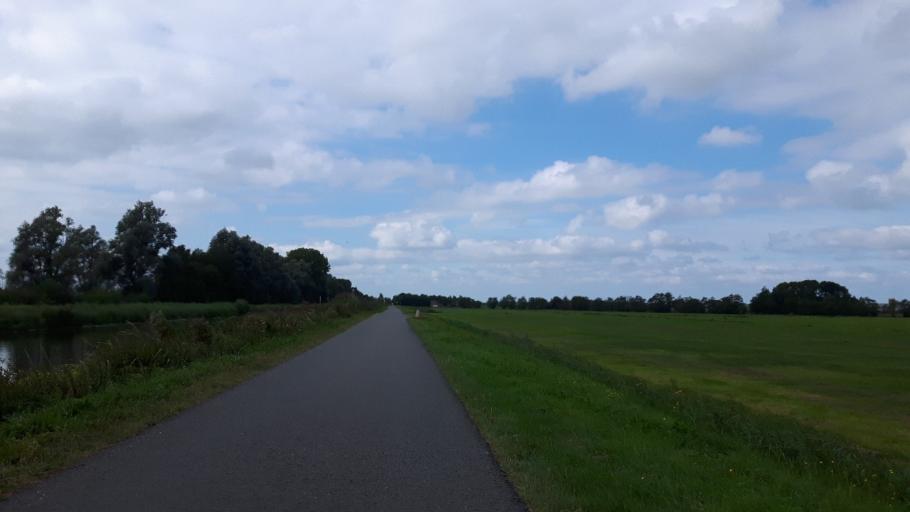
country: NL
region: Utrecht
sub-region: Gemeente De Ronde Venen
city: Mijdrecht
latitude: 52.1623
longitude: 4.9045
